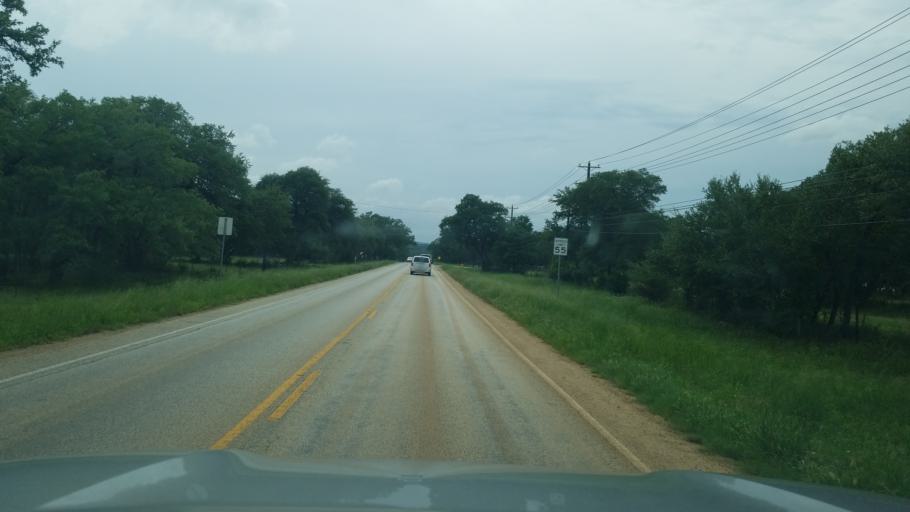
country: US
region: Texas
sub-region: Blanco County
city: Blanco
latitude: 30.0932
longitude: -98.3670
